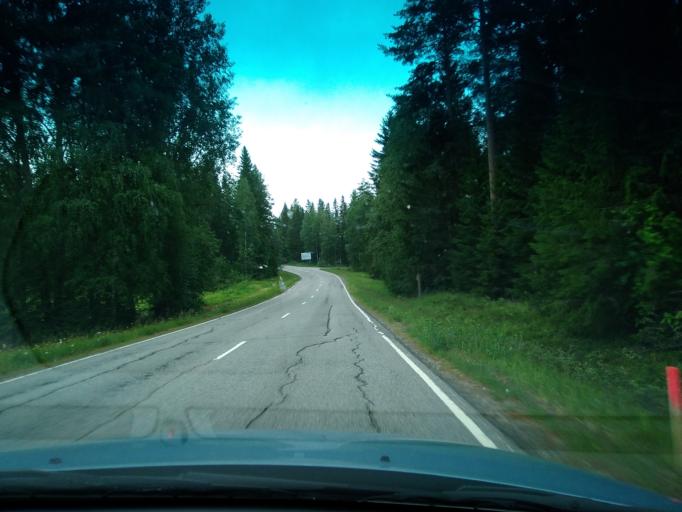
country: FI
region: Central Finland
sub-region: Keuruu
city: Multia
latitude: 62.4172
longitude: 24.7825
